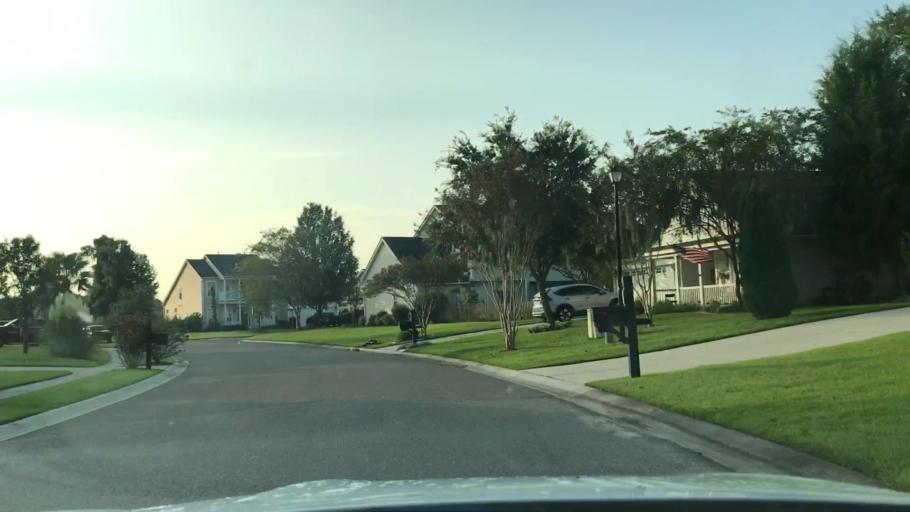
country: US
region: South Carolina
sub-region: Charleston County
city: Shell Point
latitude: 32.8366
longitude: -80.0952
